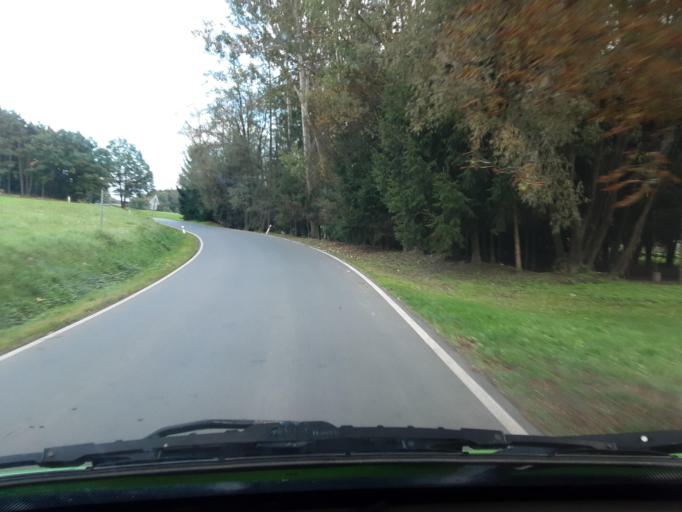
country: CZ
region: Plzensky
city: Janovice nad Uhlavou
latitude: 49.3970
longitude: 13.1500
